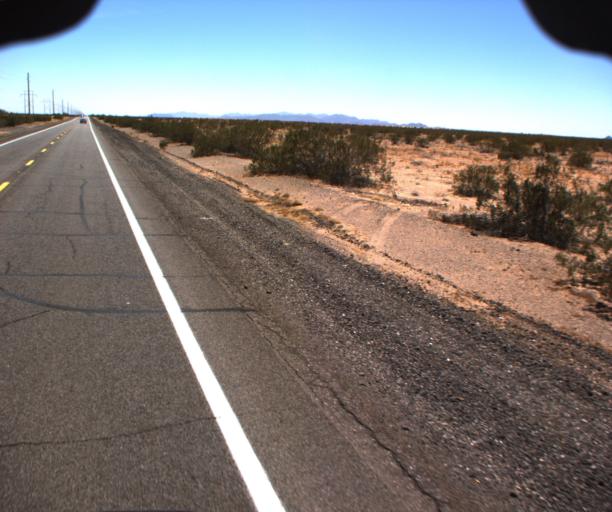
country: US
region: Arizona
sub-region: La Paz County
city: Parker
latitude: 33.9177
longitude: -114.2169
